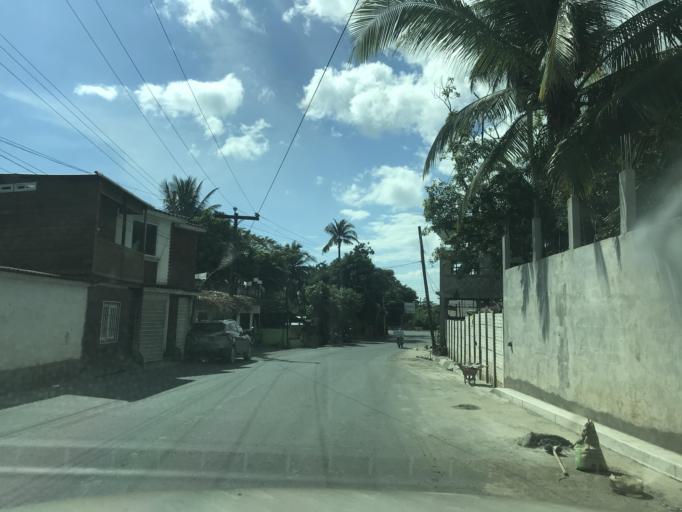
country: GT
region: Izabal
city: Morales
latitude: 15.6574
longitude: -89.0076
